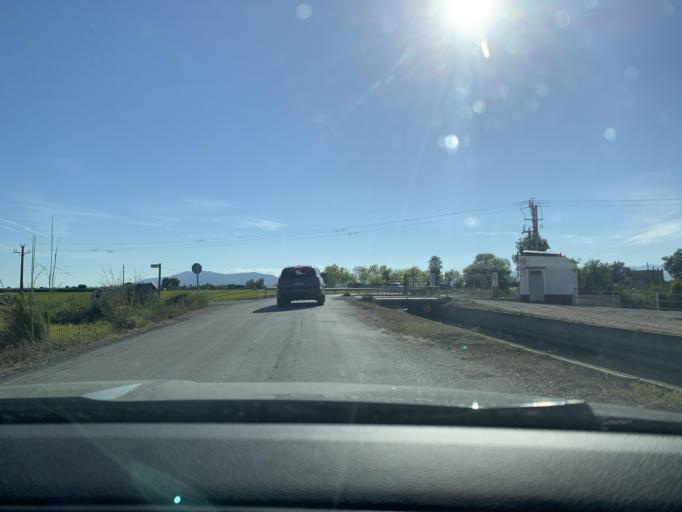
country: ES
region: Catalonia
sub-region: Provincia de Tarragona
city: Deltebre
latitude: 40.7482
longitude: 0.7361
